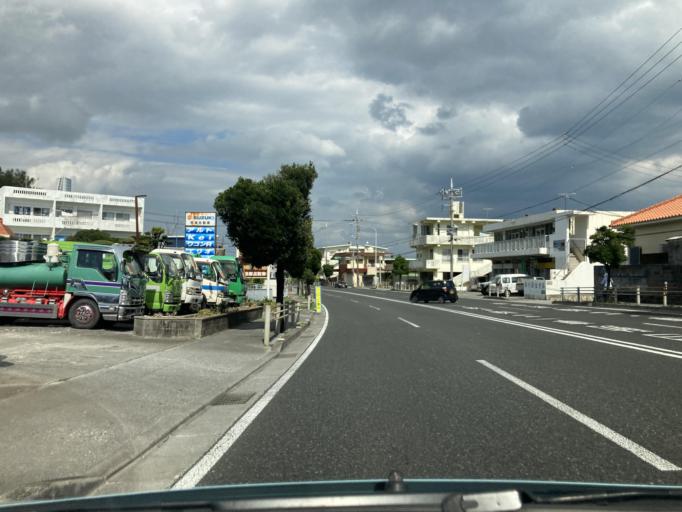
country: JP
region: Okinawa
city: Ginowan
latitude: 26.2381
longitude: 127.7758
